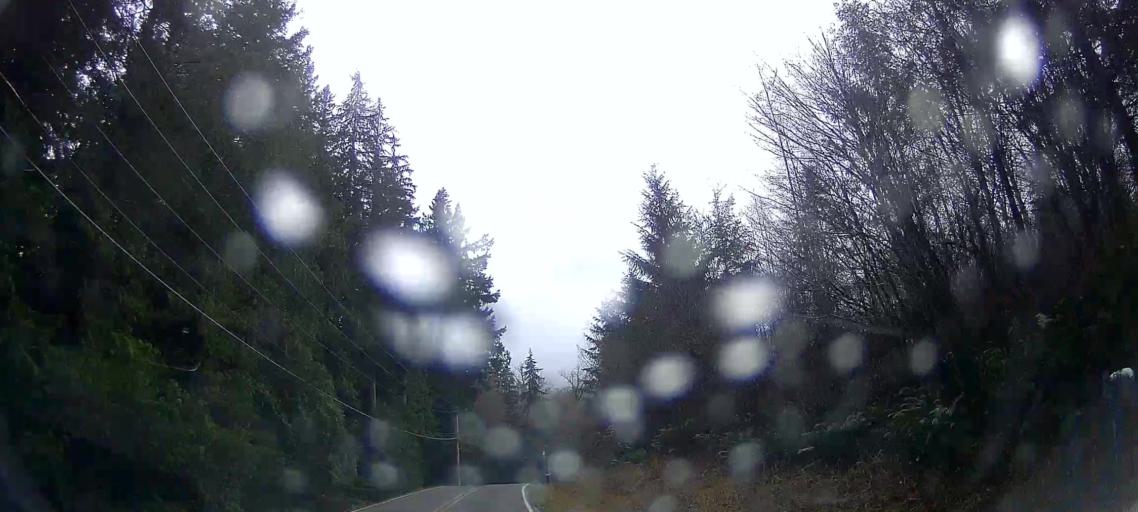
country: US
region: Washington
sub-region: Skagit County
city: Clear Lake
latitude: 48.4701
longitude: -122.1775
